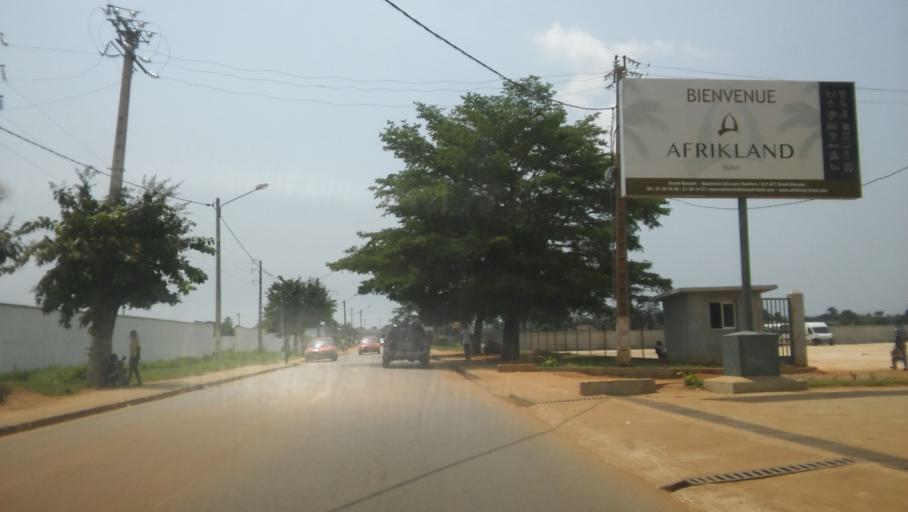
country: CI
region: Sud-Comoe
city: Grand-Bassam
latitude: 5.2023
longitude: -3.7363
